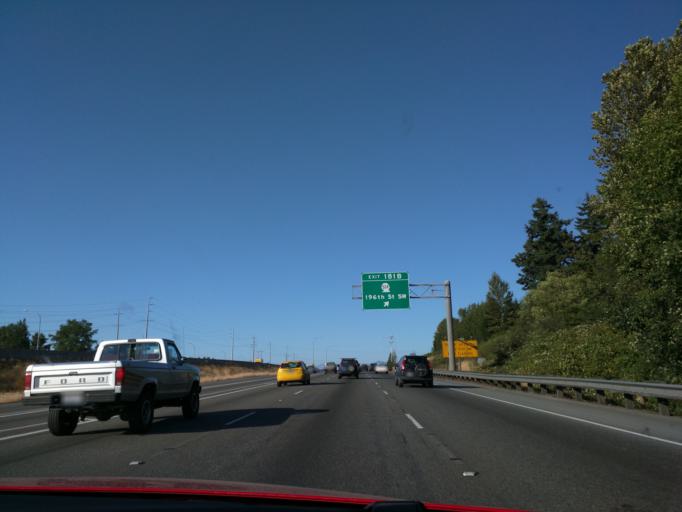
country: US
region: Washington
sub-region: Snohomish County
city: Alderwood Manor
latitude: 47.8169
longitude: -122.2862
